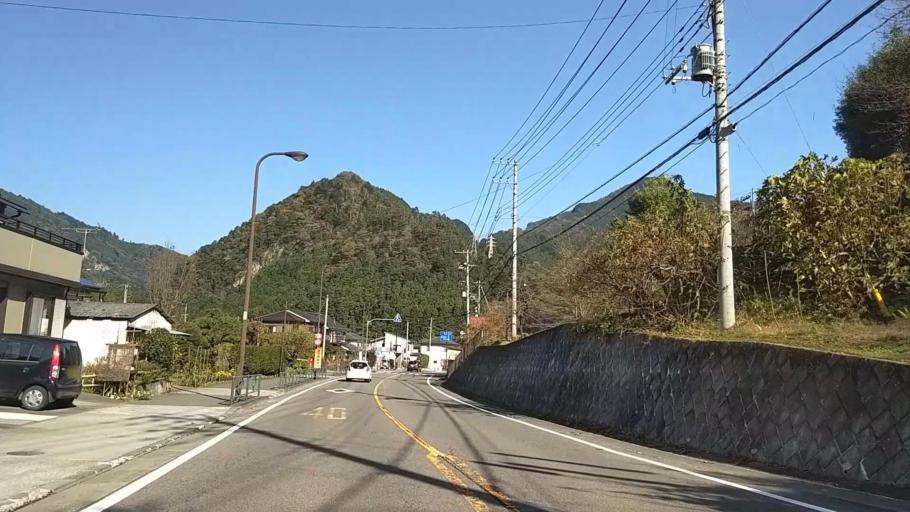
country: JP
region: Tokyo
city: Itsukaichi
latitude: 35.8016
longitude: 139.1076
